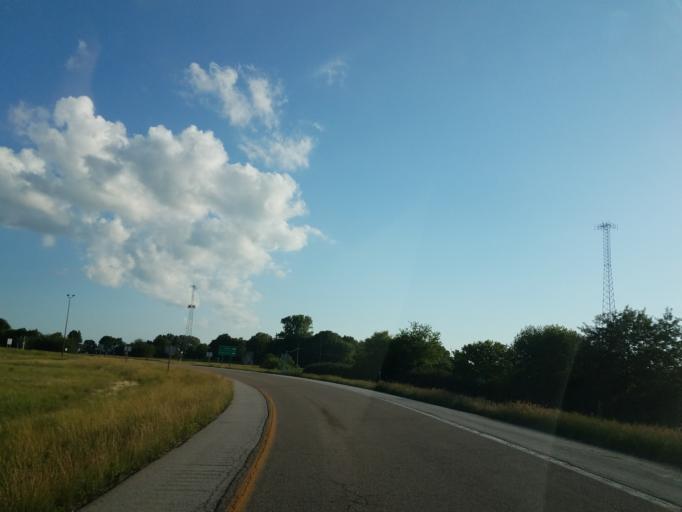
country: US
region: Illinois
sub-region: McLean County
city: Twin Grove
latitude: 40.4096
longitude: -89.0559
